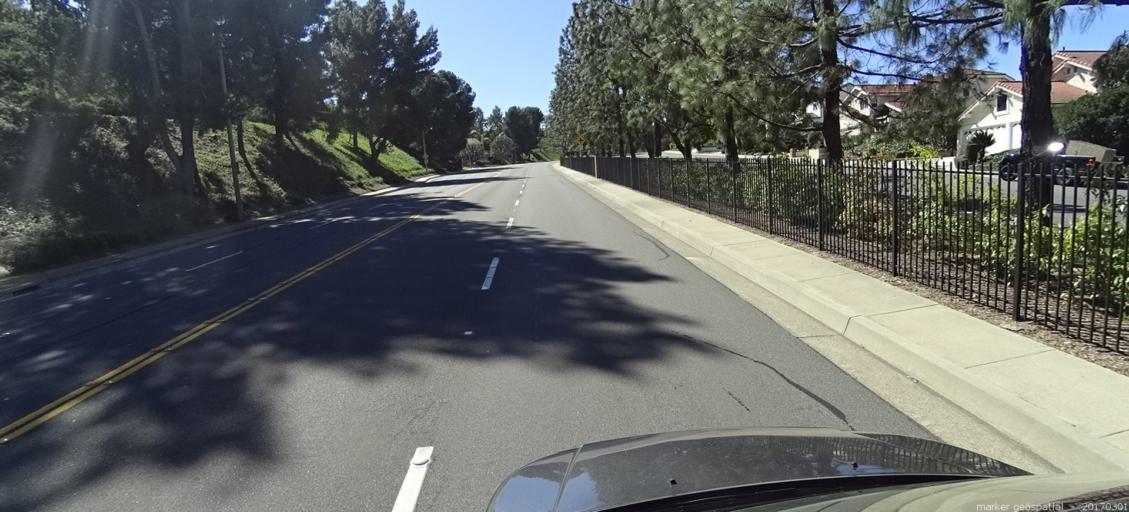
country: US
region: California
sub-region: Orange County
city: Villa Park
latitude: 33.8382
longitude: -117.8146
